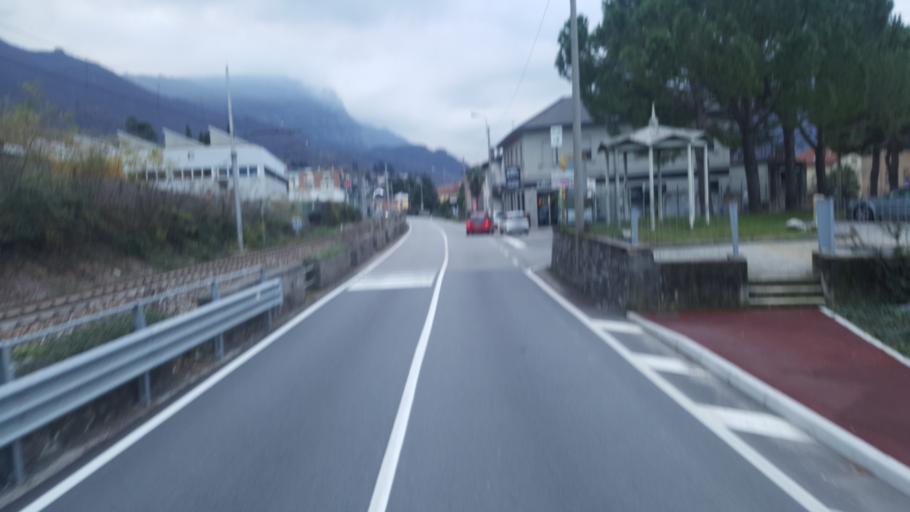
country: IT
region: Lombardy
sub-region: Provincia di Lecco
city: Mandello del Lario
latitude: 45.9187
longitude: 9.3157
